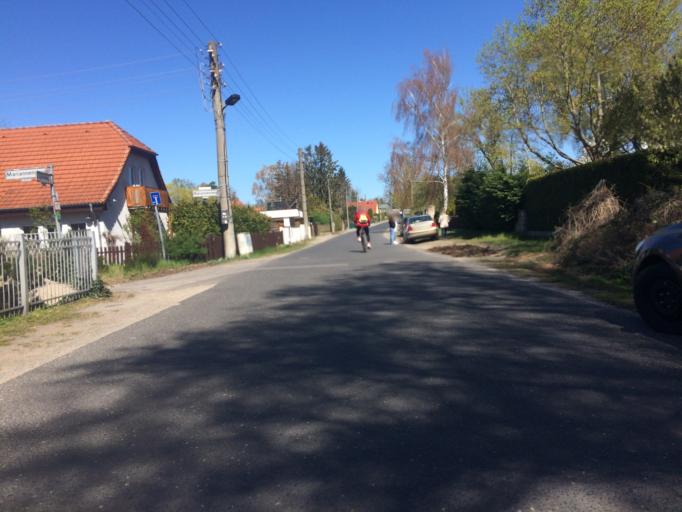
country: DE
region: Berlin
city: Rahnsdorf
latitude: 52.4298
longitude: 13.7129
